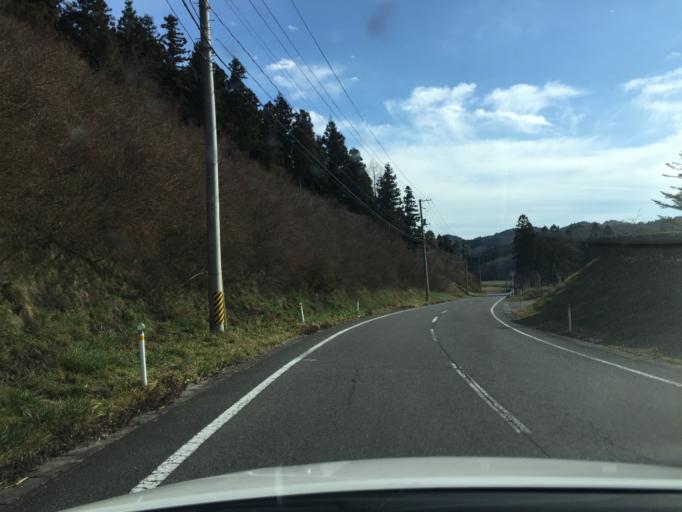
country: JP
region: Fukushima
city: Funehikimachi-funehiki
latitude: 37.2804
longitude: 140.5870
